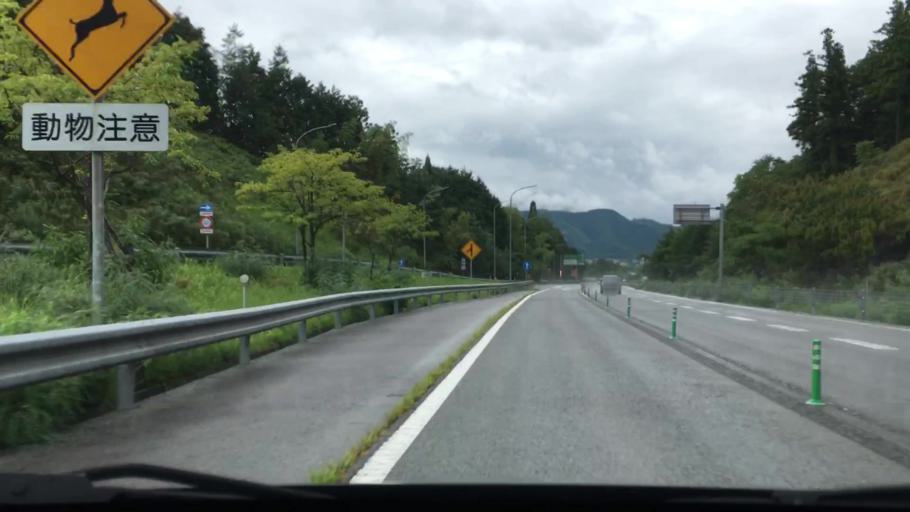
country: JP
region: Hyogo
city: Toyooka
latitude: 35.2941
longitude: 134.8251
